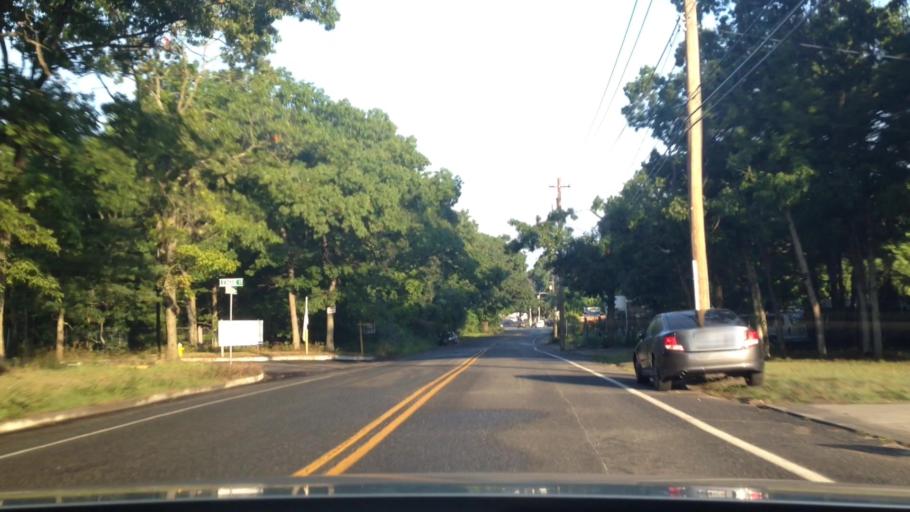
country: US
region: New York
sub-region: Suffolk County
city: Centereach
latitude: 40.8545
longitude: -73.0718
